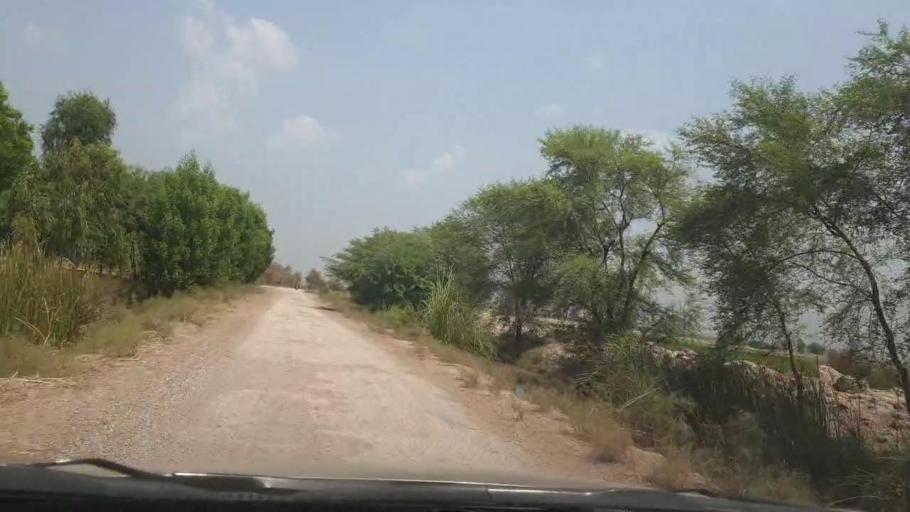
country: PK
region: Sindh
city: Ratodero
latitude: 27.6971
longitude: 68.2330
